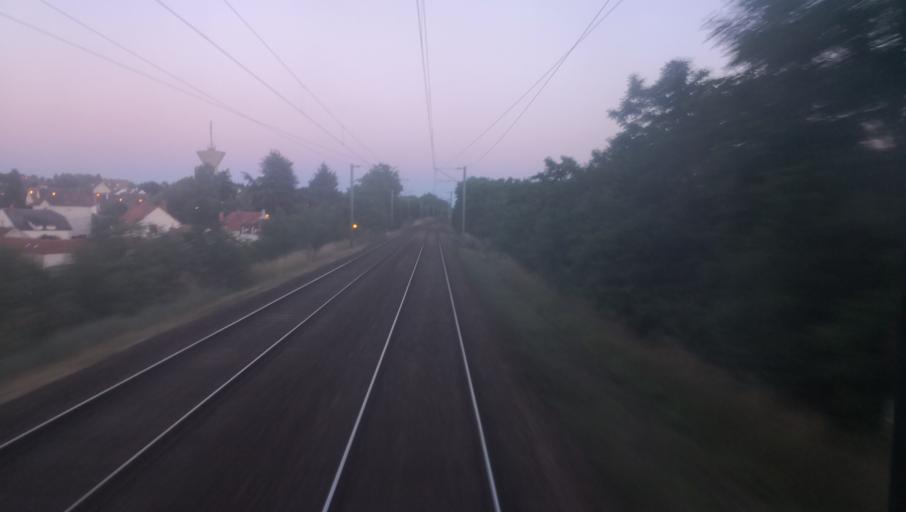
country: FR
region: Centre
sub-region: Departement du Loiret
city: Briare
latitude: 47.6395
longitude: 2.7421
